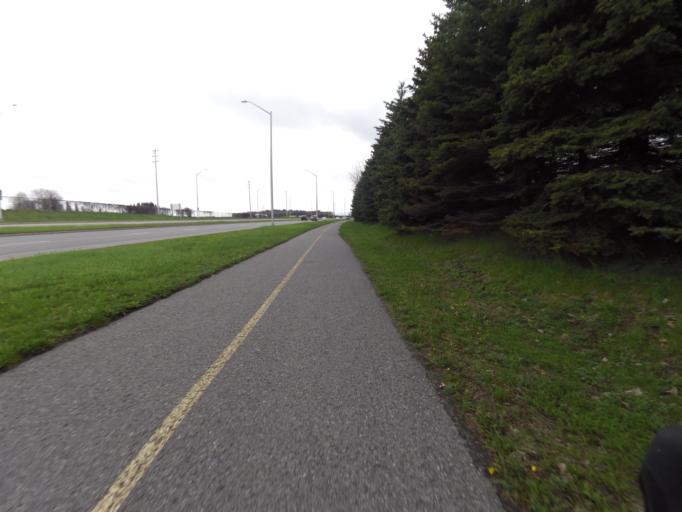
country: CA
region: Ontario
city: Bells Corners
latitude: 45.3281
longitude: -75.7506
